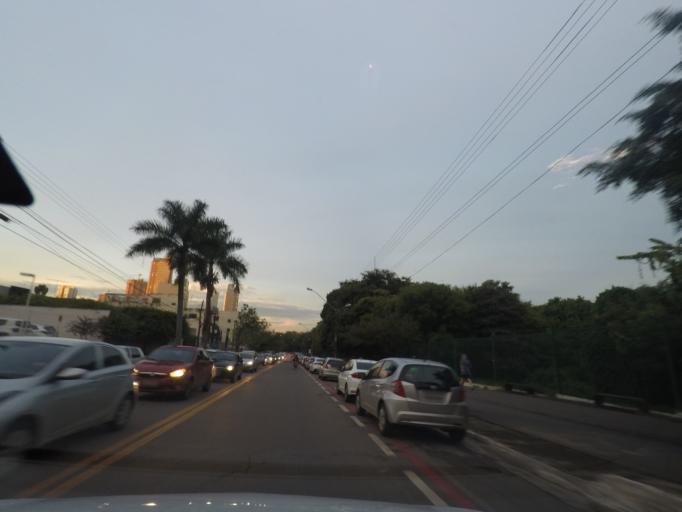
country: BR
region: Goias
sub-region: Goiania
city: Goiania
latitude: -16.7079
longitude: -49.2600
